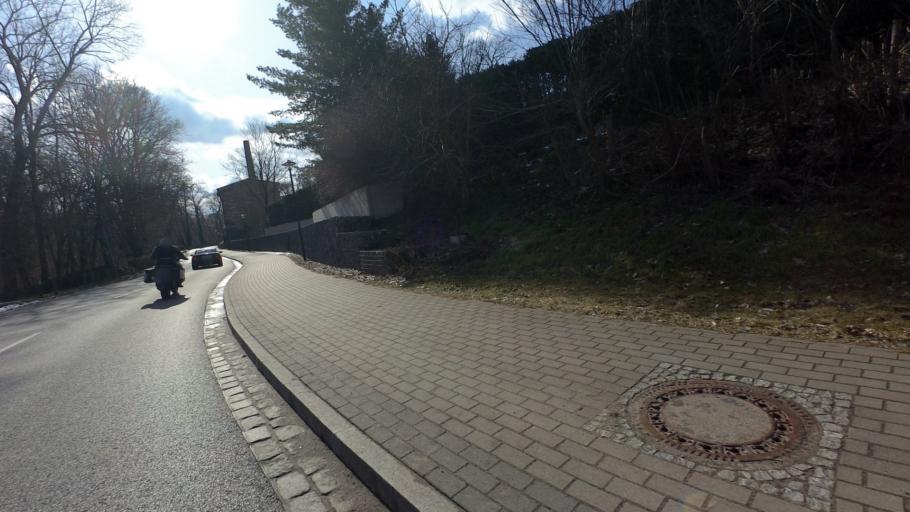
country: DE
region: Brandenburg
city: Rudnitz
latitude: 52.7610
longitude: 13.5686
